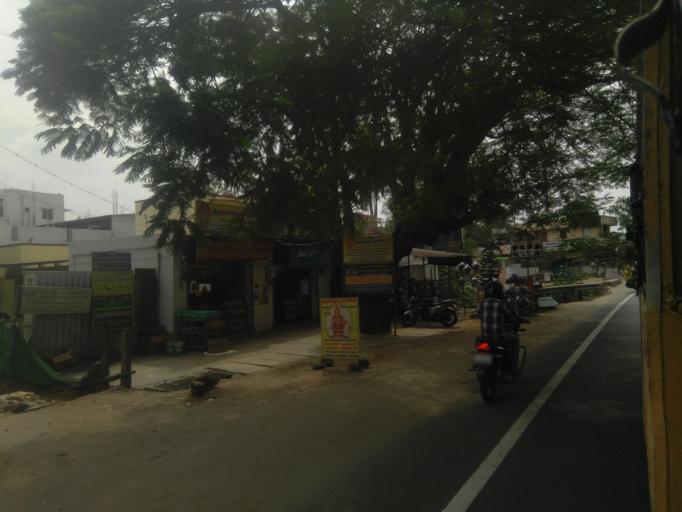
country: IN
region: Tamil Nadu
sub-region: Coimbatore
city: Irugur
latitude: 11.0078
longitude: 77.0735
